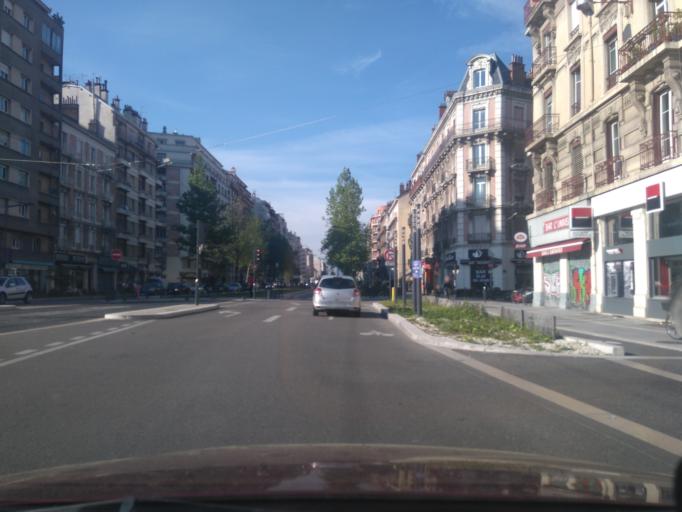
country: FR
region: Rhone-Alpes
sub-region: Departement de l'Isere
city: Grenoble
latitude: 45.1831
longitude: 5.7173
